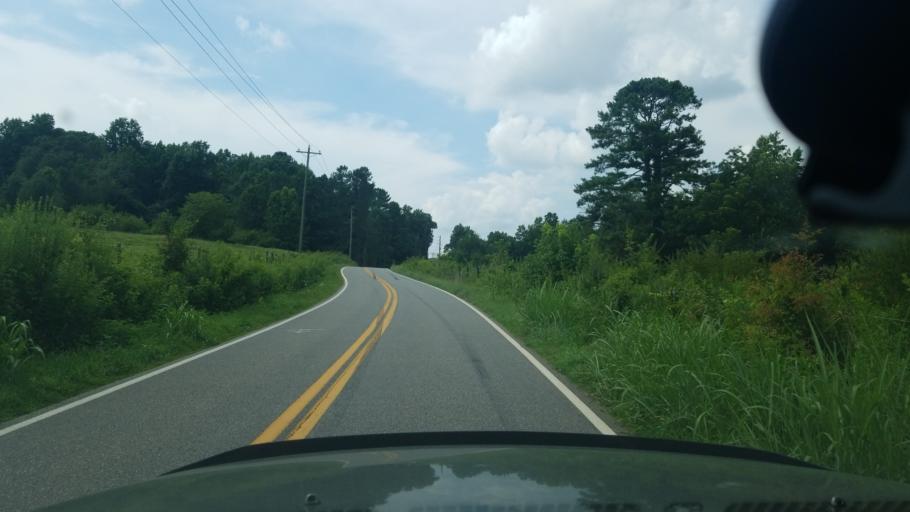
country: US
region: Georgia
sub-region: Forsyth County
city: Cumming
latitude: 34.2646
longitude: -84.1546
